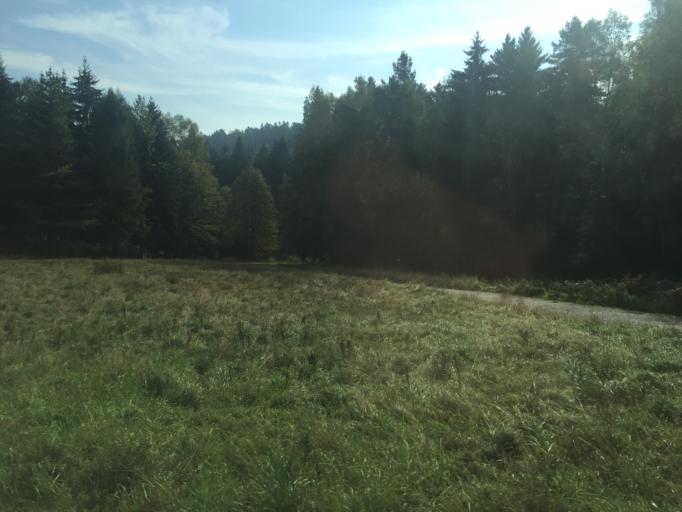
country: CZ
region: Ustecky
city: Ceska Kamenice
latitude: 50.8459
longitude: 14.3914
